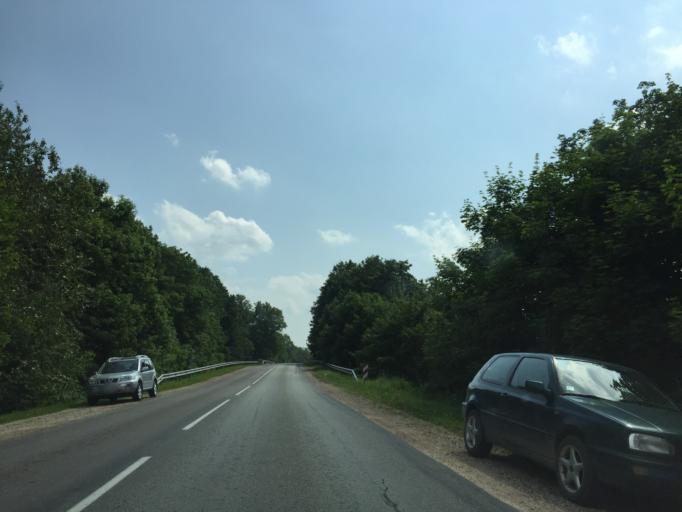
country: LV
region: Jelgava
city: Jelgava
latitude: 56.6897
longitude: 23.7193
